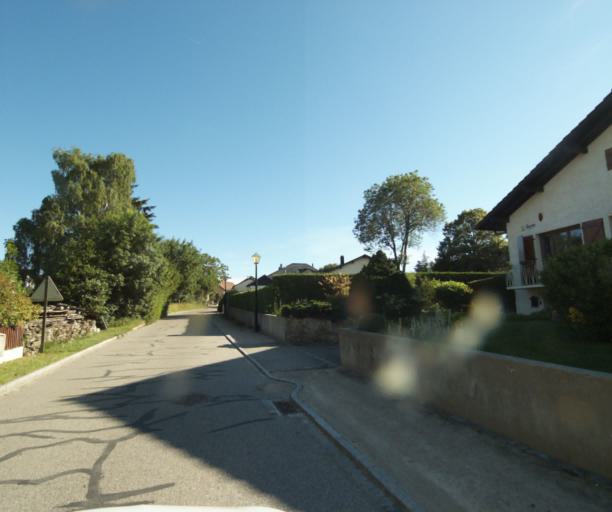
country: FR
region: Rhone-Alpes
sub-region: Departement de la Haute-Savoie
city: Massongy
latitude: 46.3251
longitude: 6.3265
